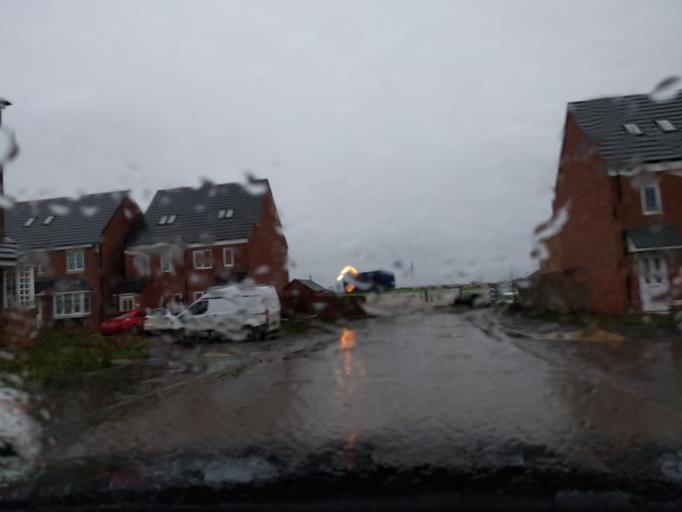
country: GB
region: England
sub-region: Northumberland
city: Newbiggin-by-the-Sea
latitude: 55.1817
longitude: -1.5456
